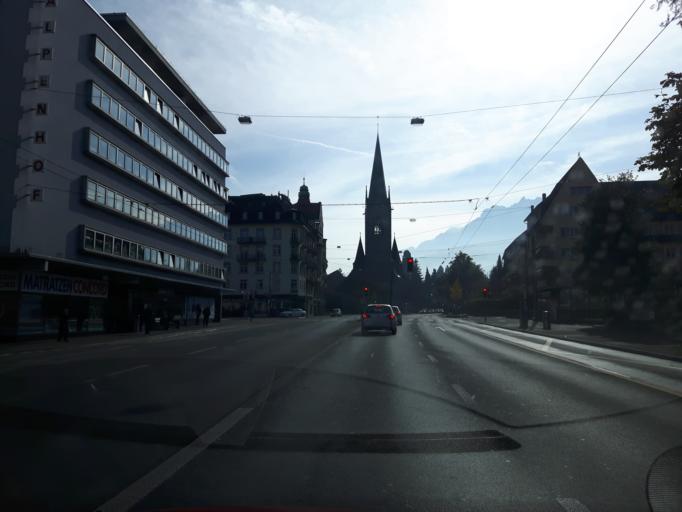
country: CH
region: Lucerne
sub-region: Lucerne-Stadt District
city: Luzern
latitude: 47.0438
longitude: 8.3037
